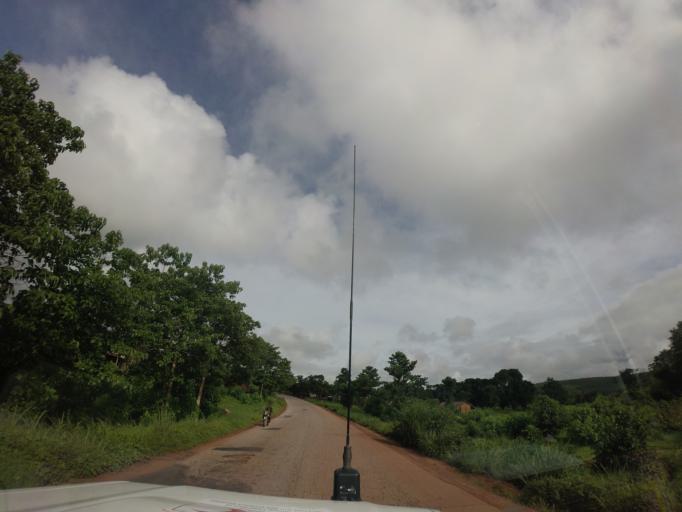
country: GN
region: Kindia
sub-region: Coyah
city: Coyah
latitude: 9.8340
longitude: -13.2212
